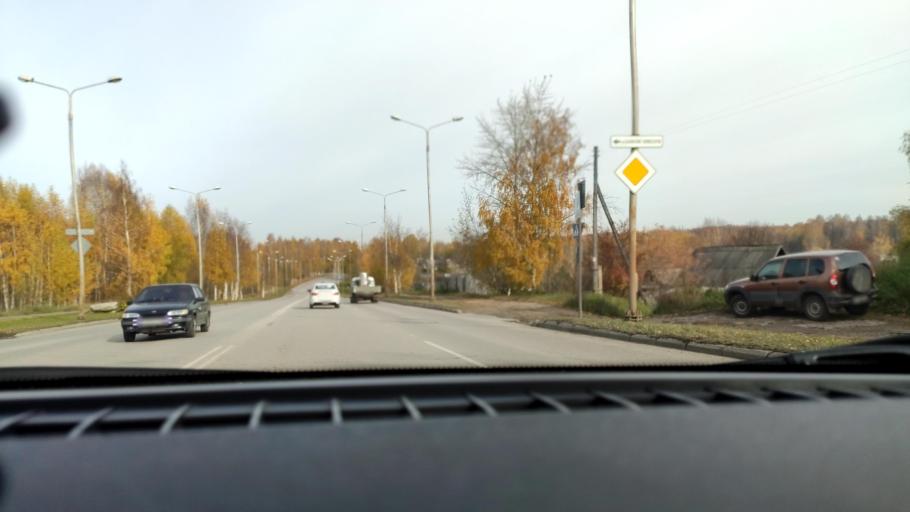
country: RU
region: Perm
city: Perm
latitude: 58.0945
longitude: 56.3841
